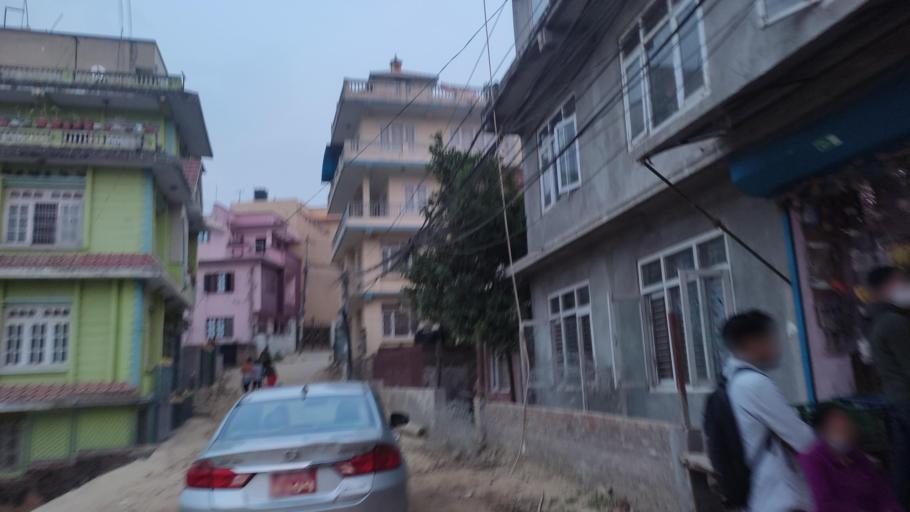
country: NP
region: Central Region
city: Kirtipur
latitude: 27.6733
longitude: 85.2833
